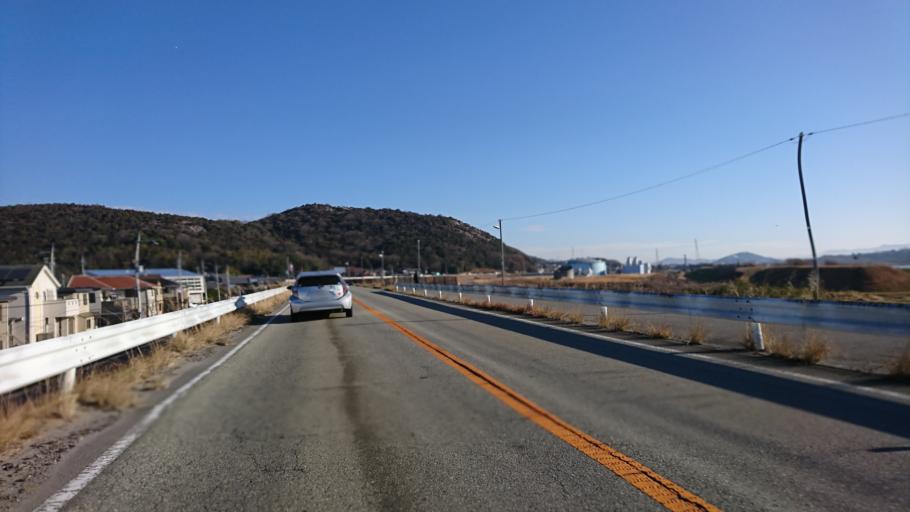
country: JP
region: Hyogo
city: Kakogawacho-honmachi
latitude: 34.7832
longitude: 134.8454
